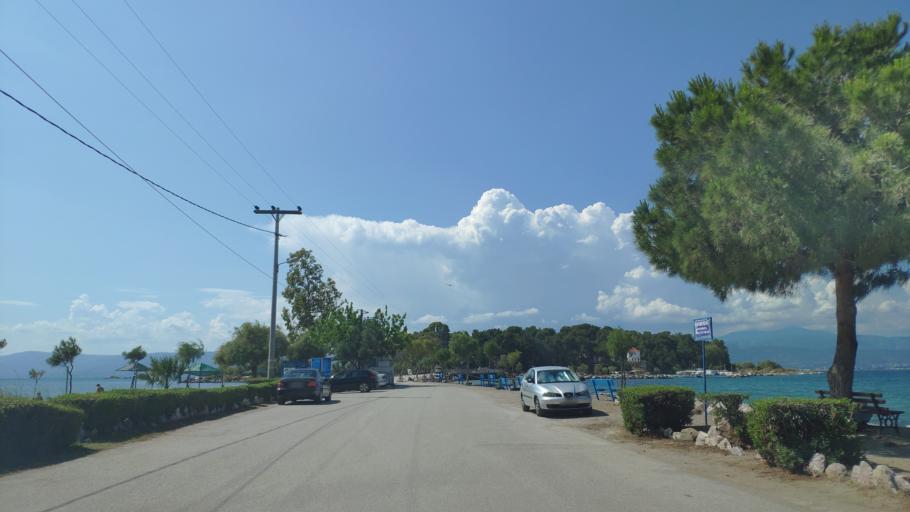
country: GR
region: Central Greece
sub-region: Nomos Evvoias
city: Eretria
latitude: 38.3882
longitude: 23.8006
